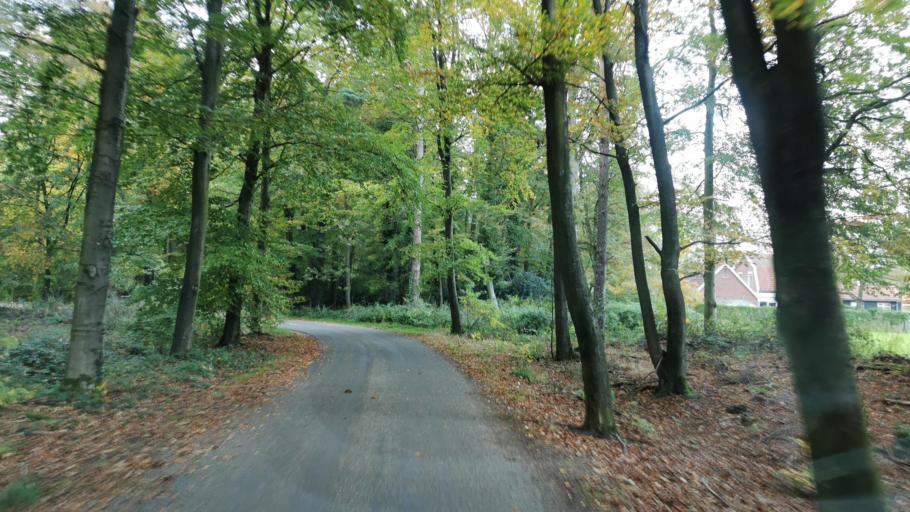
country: NL
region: Overijssel
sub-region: Gemeente Oldenzaal
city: Oldenzaal
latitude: 52.3099
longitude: 6.9741
